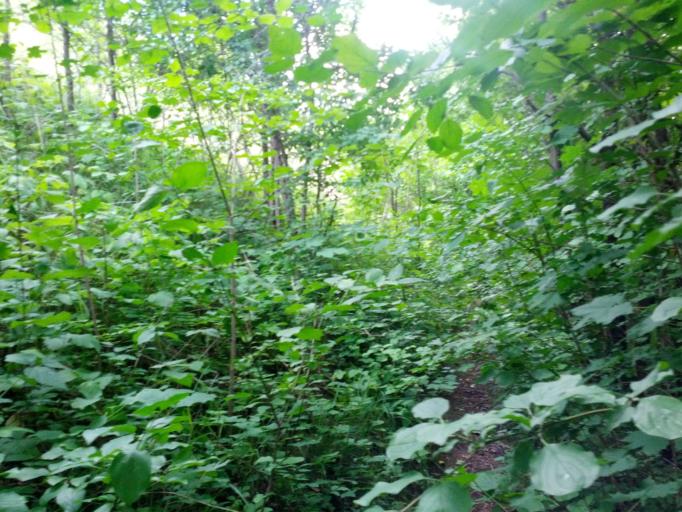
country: DE
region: Thuringia
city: Eisenach
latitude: 50.9841
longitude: 10.3046
